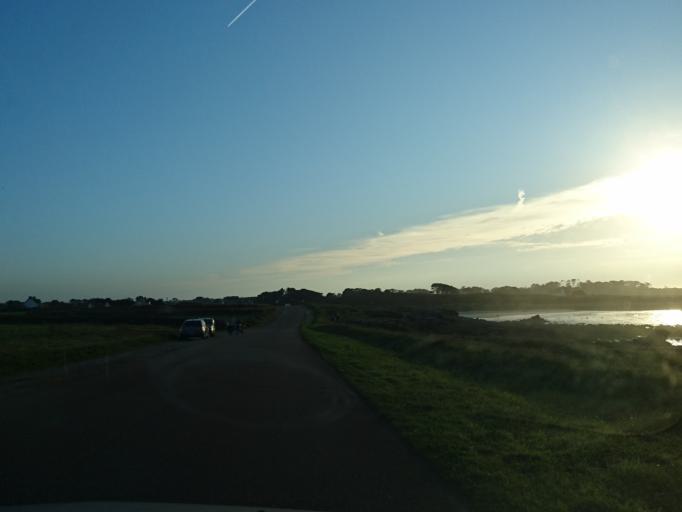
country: FR
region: Brittany
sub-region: Departement du Finistere
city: Landunvez
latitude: 48.5354
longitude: -4.7489
